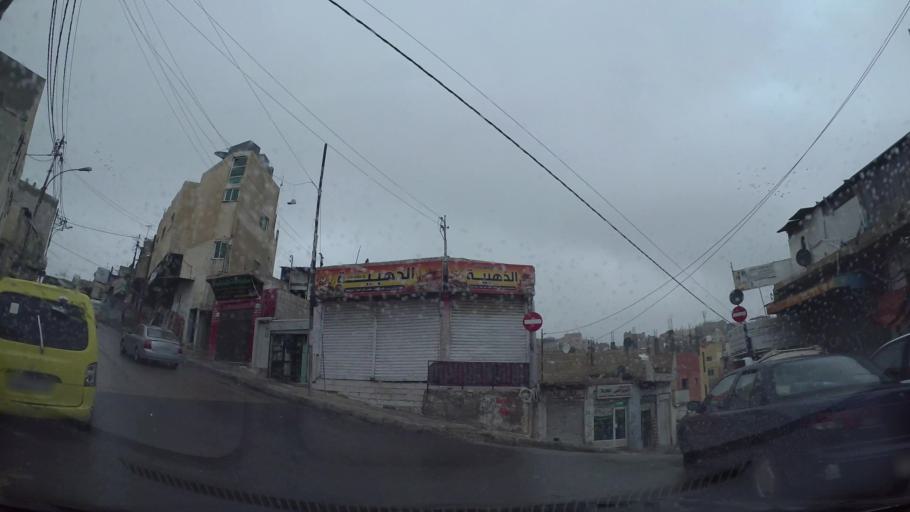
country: JO
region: Amman
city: Amman
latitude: 31.9695
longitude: 35.9259
